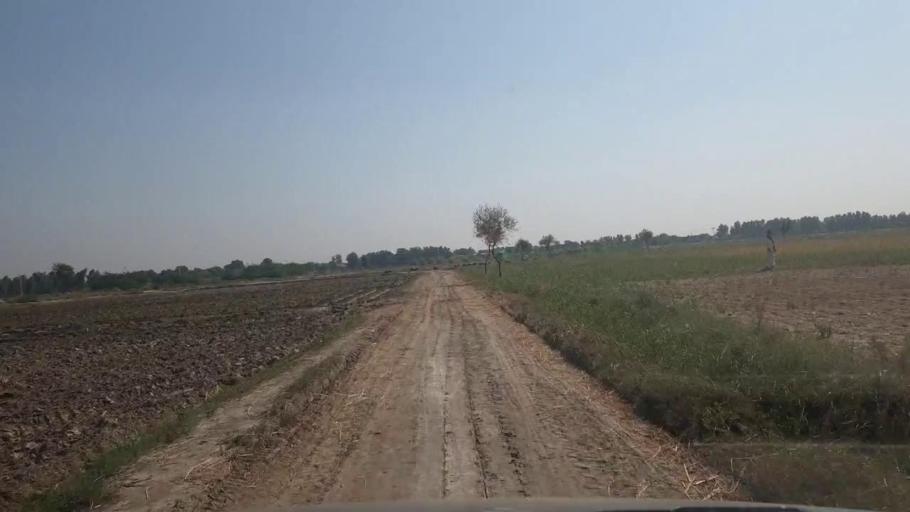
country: PK
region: Sindh
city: Badin
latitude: 24.6800
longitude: 68.8978
